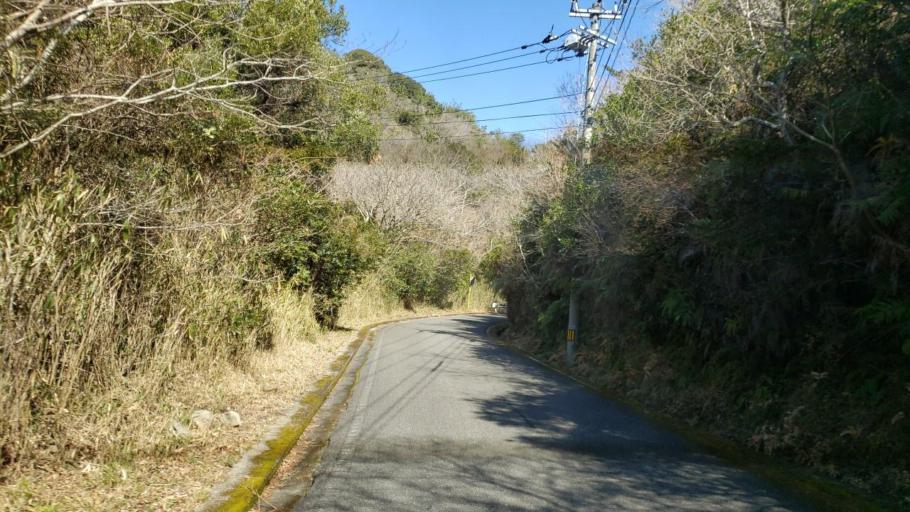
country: JP
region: Tokushima
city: Narutocho-mitsuishi
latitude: 34.1954
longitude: 134.5538
